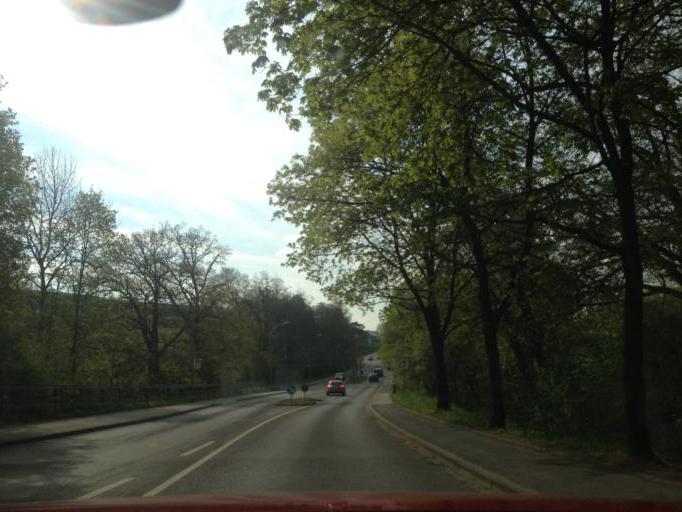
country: DE
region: Bavaria
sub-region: Regierungsbezirk Mittelfranken
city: Lauf an der Pegnitz
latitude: 49.5139
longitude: 11.2641
